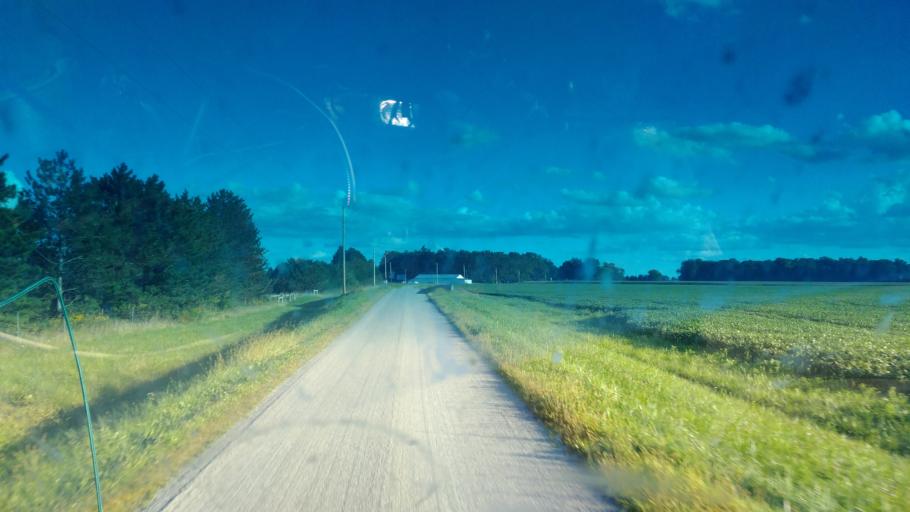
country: US
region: Ohio
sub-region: Wyandot County
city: Carey
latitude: 40.8985
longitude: -83.3444
